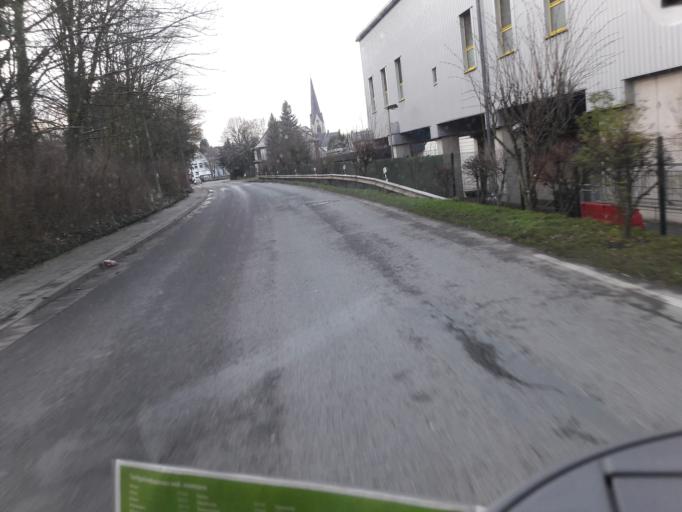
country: DE
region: Lower Saxony
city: Buckeburg
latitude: 52.2349
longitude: 9.0455
